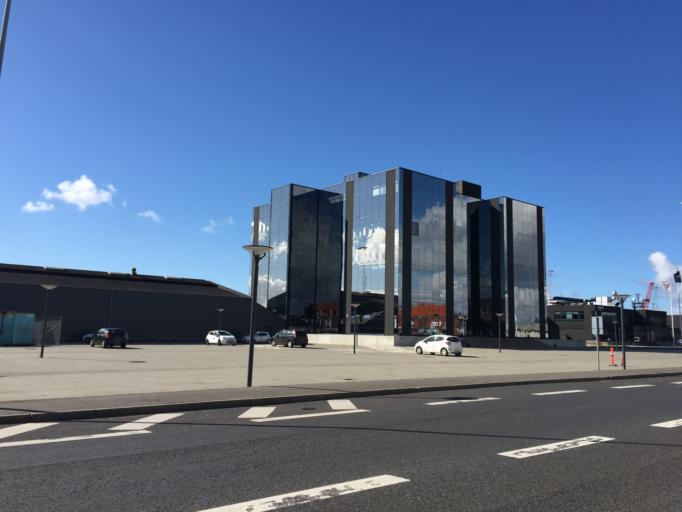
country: DK
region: South Denmark
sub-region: Esbjerg Kommune
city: Esbjerg
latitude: 55.4687
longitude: 8.4359
